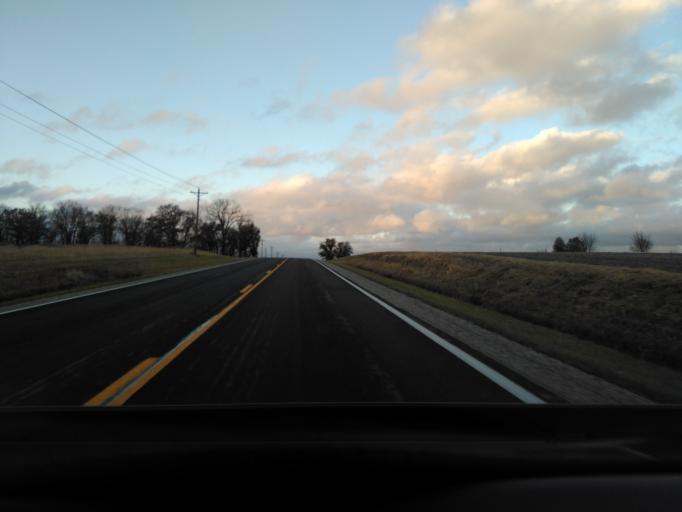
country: US
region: Illinois
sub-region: Effingham County
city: Altamont
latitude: 38.9838
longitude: -88.7489
